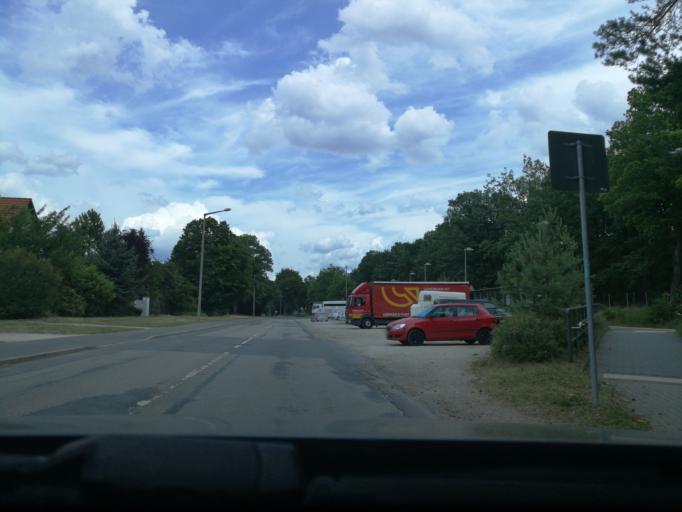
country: DE
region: Bavaria
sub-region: Regierungsbezirk Mittelfranken
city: Furth
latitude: 49.4690
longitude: 10.9712
